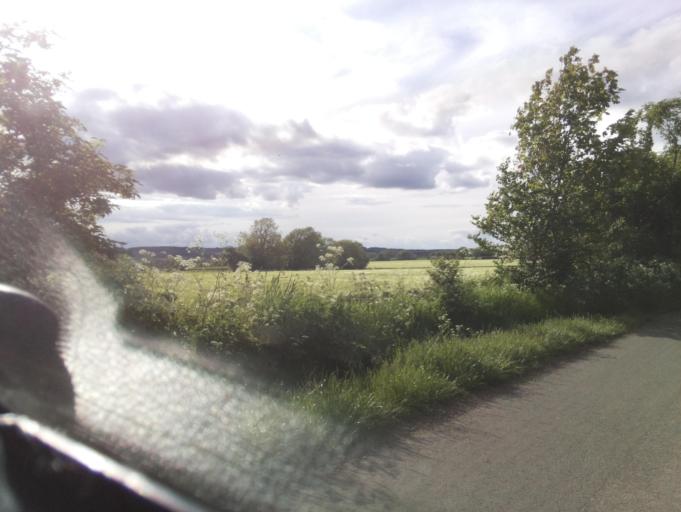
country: GB
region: England
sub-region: Gloucestershire
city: Donnington
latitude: 51.9491
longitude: -1.7817
